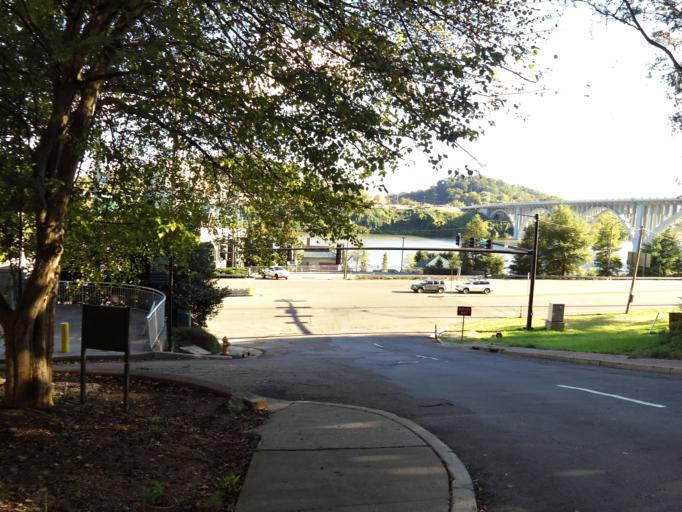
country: US
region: Tennessee
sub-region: Knox County
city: Knoxville
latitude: 35.9598
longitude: -83.9176
